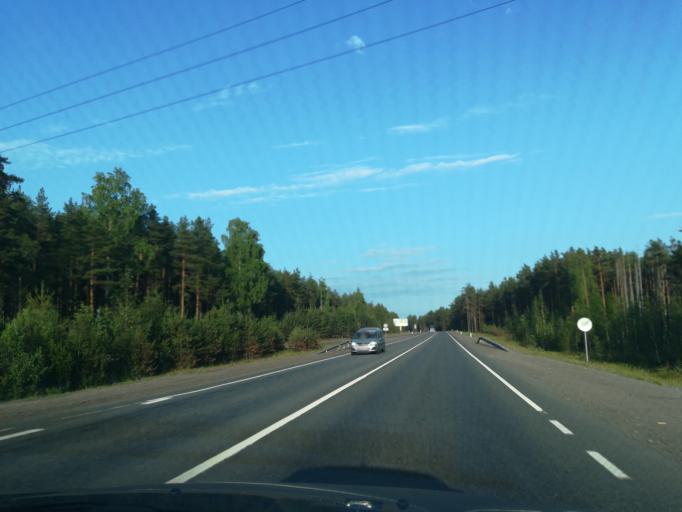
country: RU
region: Leningrad
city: Vyborg
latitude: 60.6632
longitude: 28.9345
